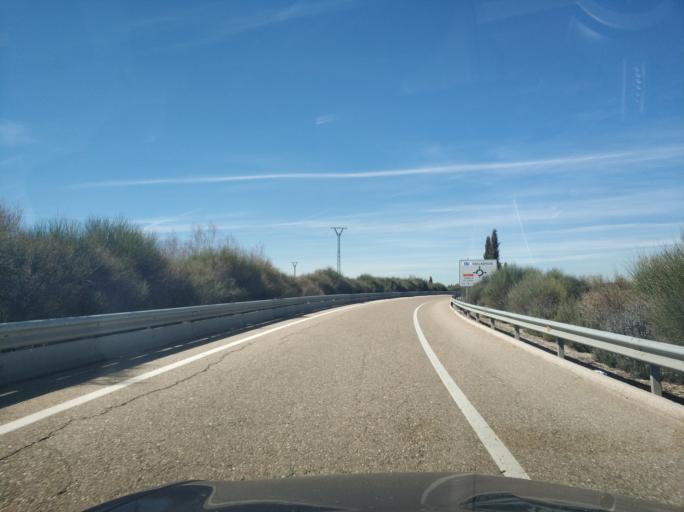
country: ES
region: Castille and Leon
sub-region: Provincia de Valladolid
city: Tudela de Duero
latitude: 41.5873
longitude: -4.5525
